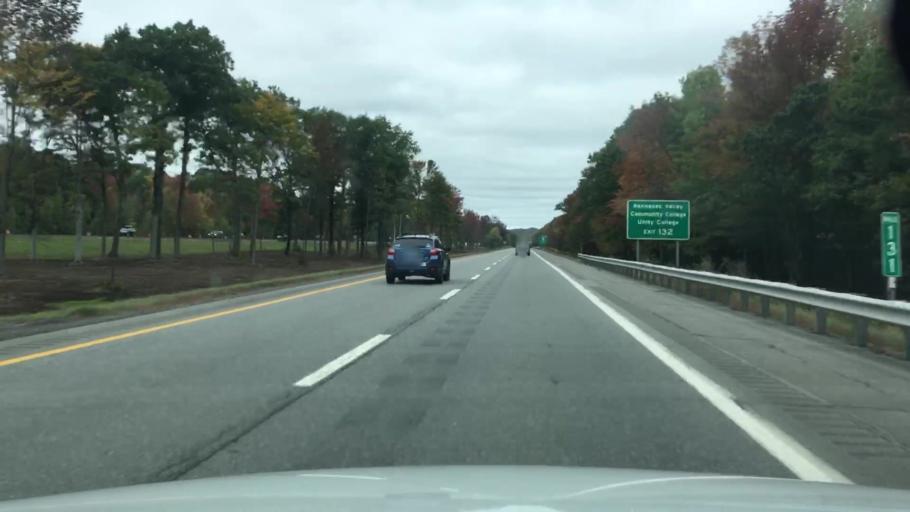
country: US
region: Maine
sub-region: Kennebec County
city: Waterville
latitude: 44.5770
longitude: -69.6297
